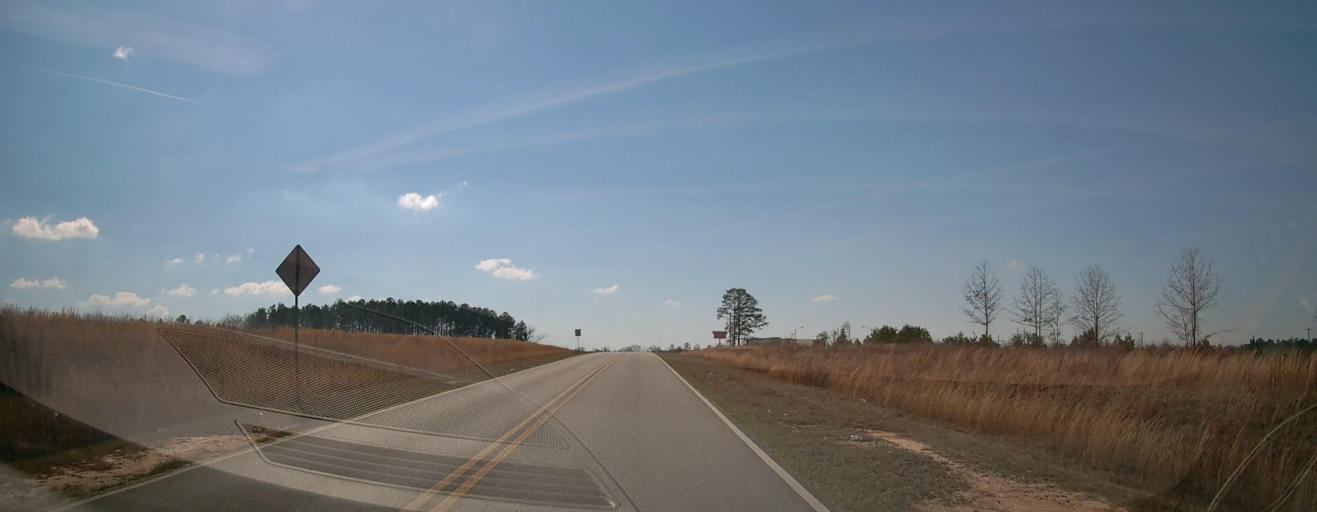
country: US
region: Georgia
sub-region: Wilkinson County
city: Gordon
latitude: 32.8965
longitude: -83.3032
